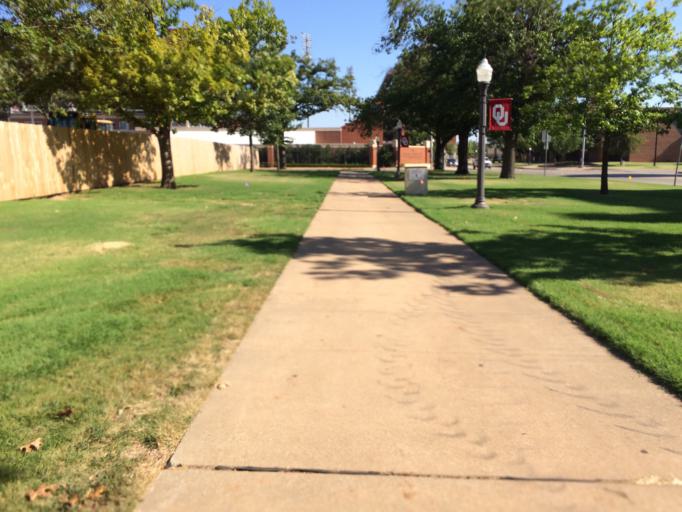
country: US
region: Oklahoma
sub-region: Cleveland County
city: Norman
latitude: 35.2032
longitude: -97.4416
